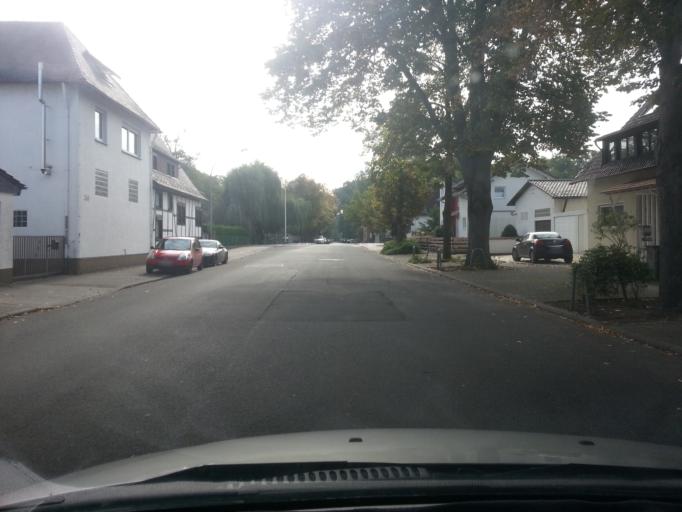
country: DE
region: Rheinland-Pfalz
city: Hassloch
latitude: 49.3482
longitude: 8.2618
